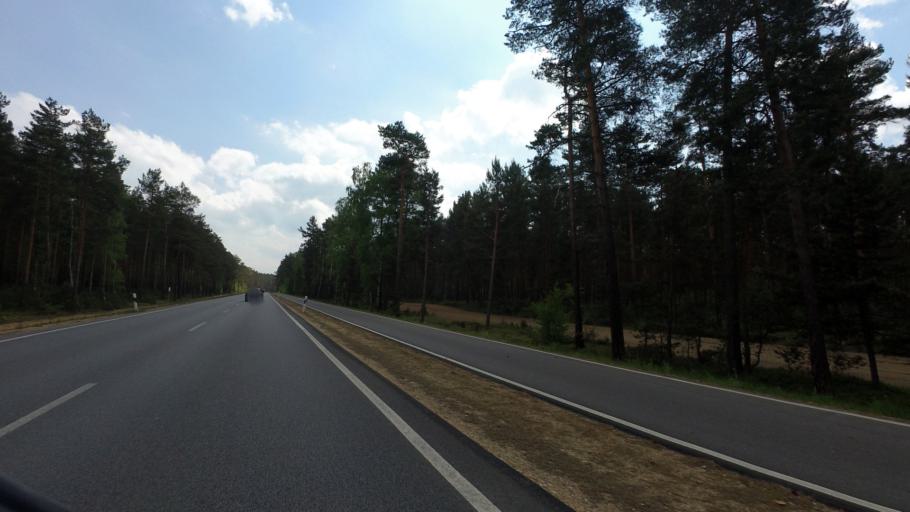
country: DE
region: Saxony
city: Rietschen
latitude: 51.4262
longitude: 14.7876
